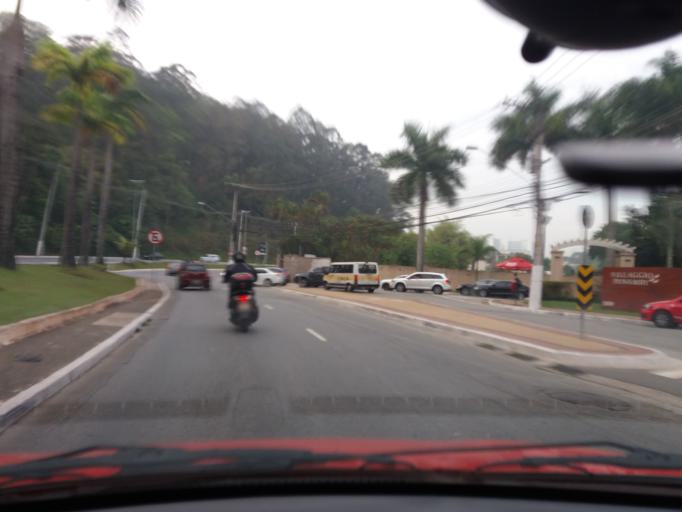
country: BR
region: Sao Paulo
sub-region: Taboao Da Serra
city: Taboao da Serra
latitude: -23.6367
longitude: -46.7271
